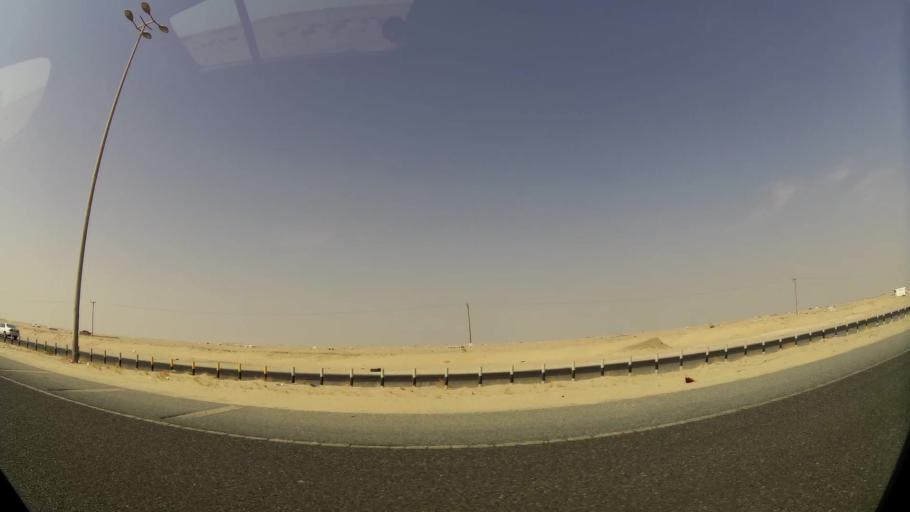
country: KW
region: Al Ahmadi
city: Al Wafrah
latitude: 28.8334
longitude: 48.0552
